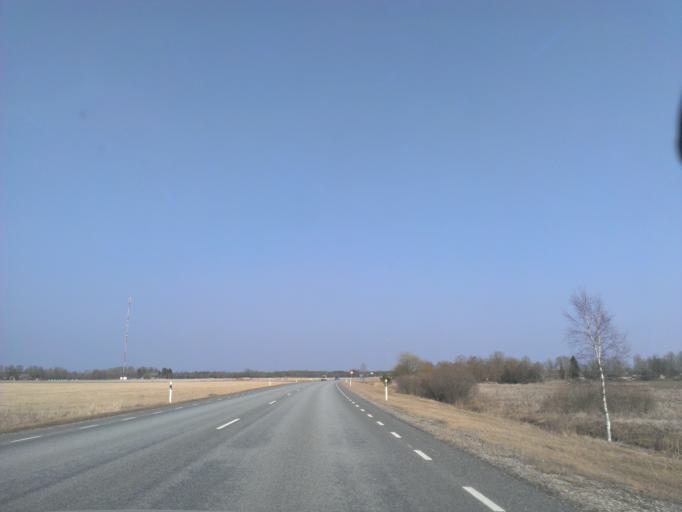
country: EE
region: Saare
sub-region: Orissaare vald
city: Orissaare
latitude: 58.5100
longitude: 22.8729
